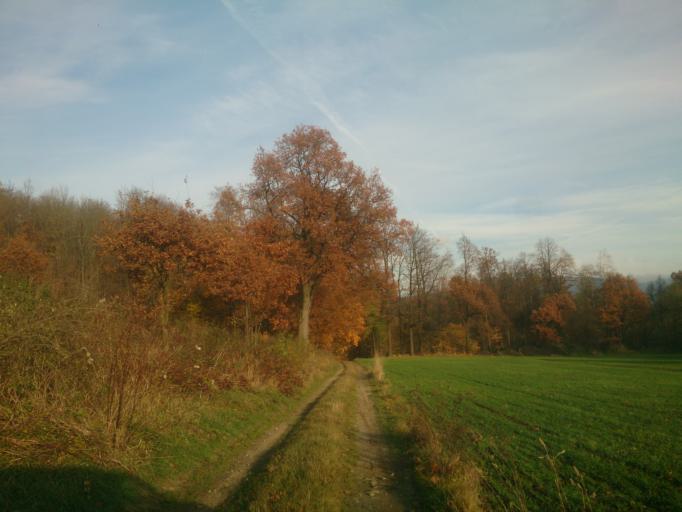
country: PL
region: Lower Silesian Voivodeship
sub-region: Powiat jeleniogorski
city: Kowary
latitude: 50.8046
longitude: 15.8096
